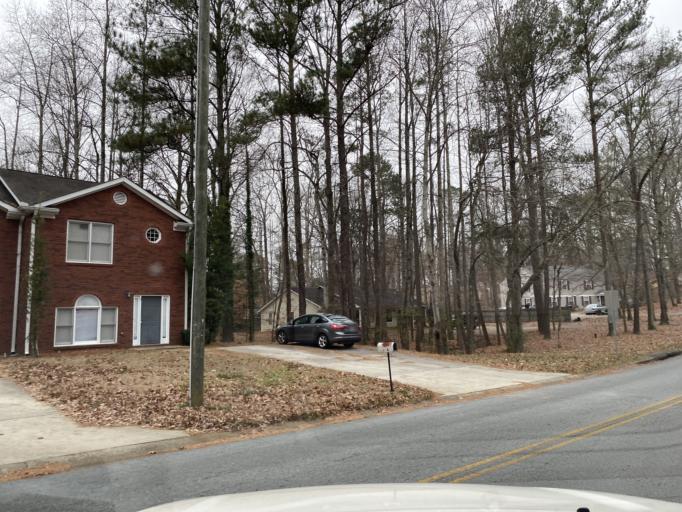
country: US
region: Georgia
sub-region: Cobb County
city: Fair Oaks
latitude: 33.9181
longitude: -84.5718
